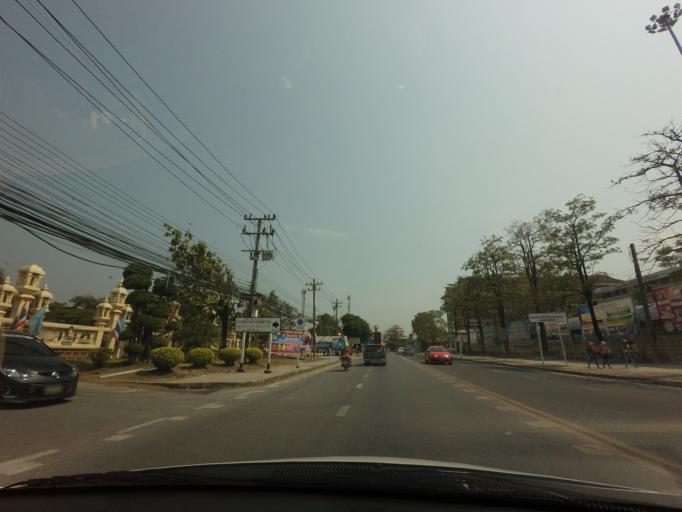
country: TH
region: Nakhon Pathom
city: Sam Phran
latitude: 13.7407
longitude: 100.2595
